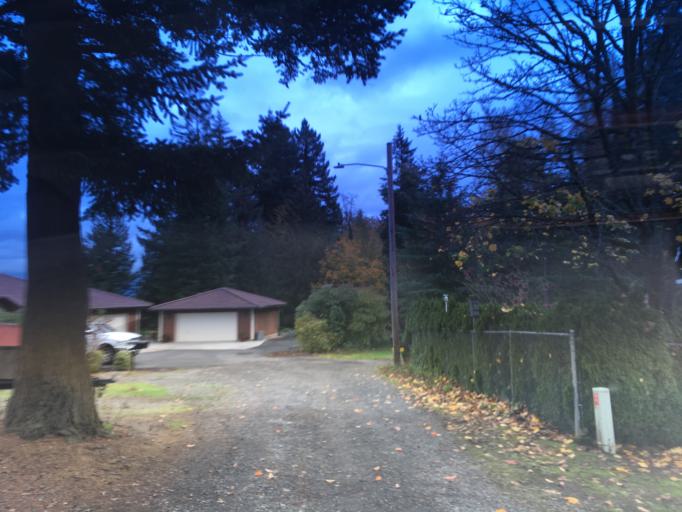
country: US
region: Oregon
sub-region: Multnomah County
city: Fairview
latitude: 45.5403
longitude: -122.4292
